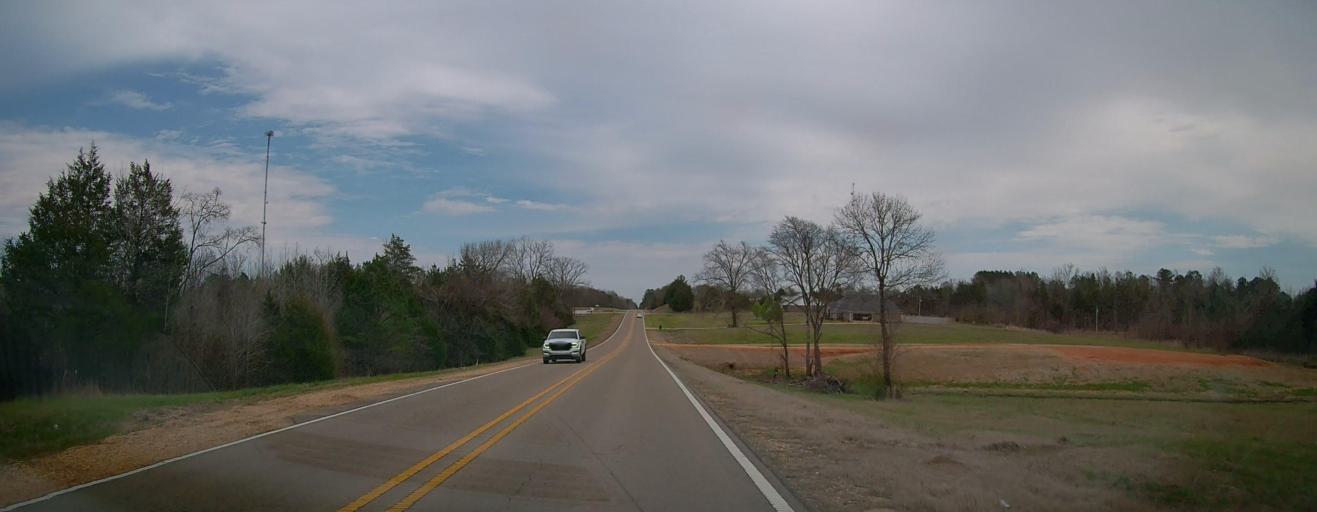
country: US
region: Mississippi
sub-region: Itawamba County
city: Mantachie
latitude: 34.2614
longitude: -88.5260
